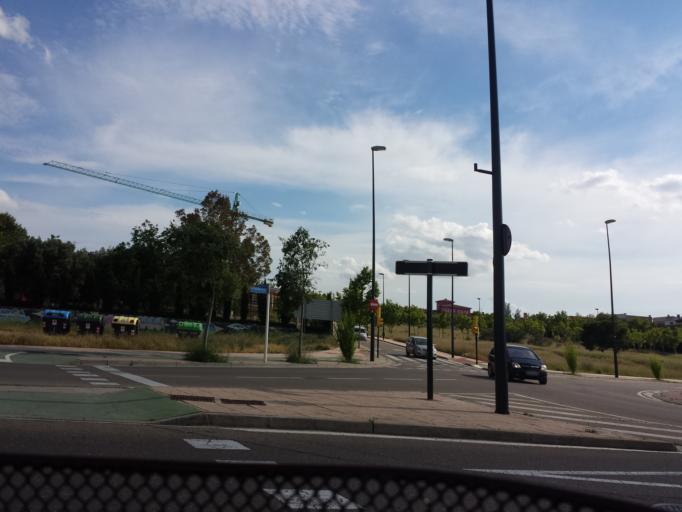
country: ES
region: Aragon
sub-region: Provincia de Zaragoza
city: Montecanal
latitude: 41.6326
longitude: -0.9295
